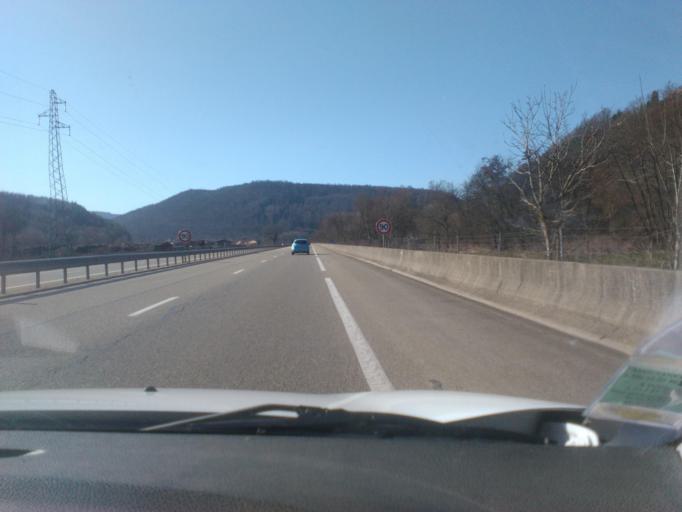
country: FR
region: Alsace
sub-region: Departement du Bas-Rhin
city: Still
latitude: 48.5345
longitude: 7.3983
